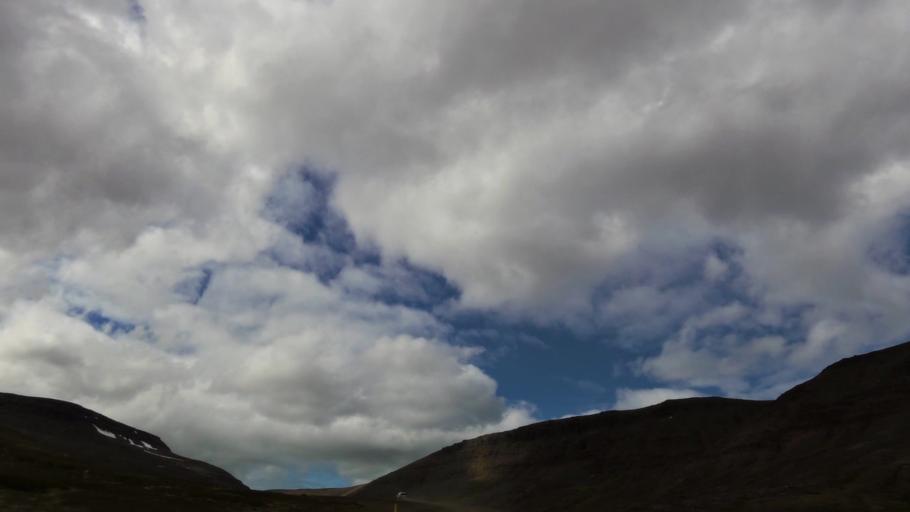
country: IS
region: Westfjords
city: Isafjoerdur
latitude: 66.1607
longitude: -23.3010
